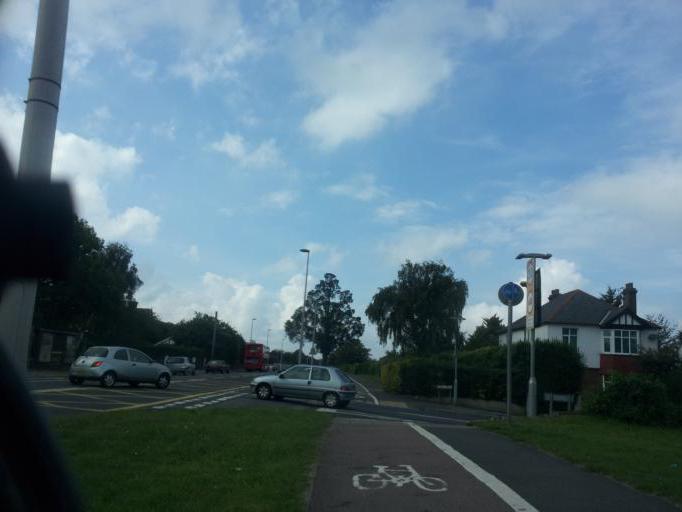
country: GB
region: England
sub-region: Kent
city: Rainham
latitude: 51.3673
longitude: 0.5900
